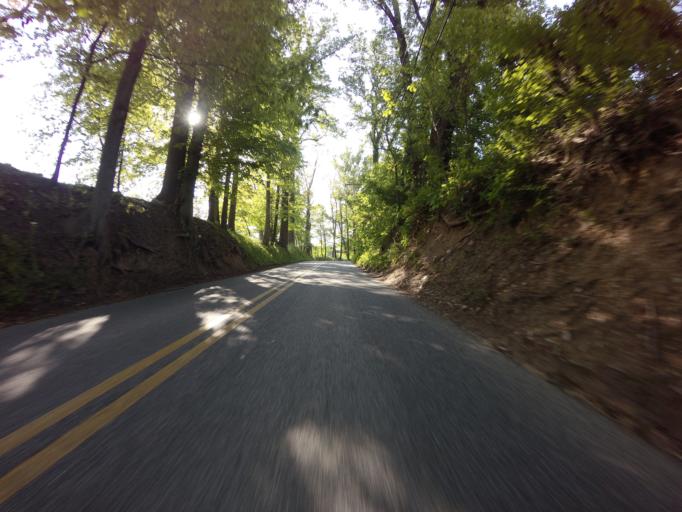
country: US
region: Maryland
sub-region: Baltimore County
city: Hunt Valley
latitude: 39.5051
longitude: -76.6987
